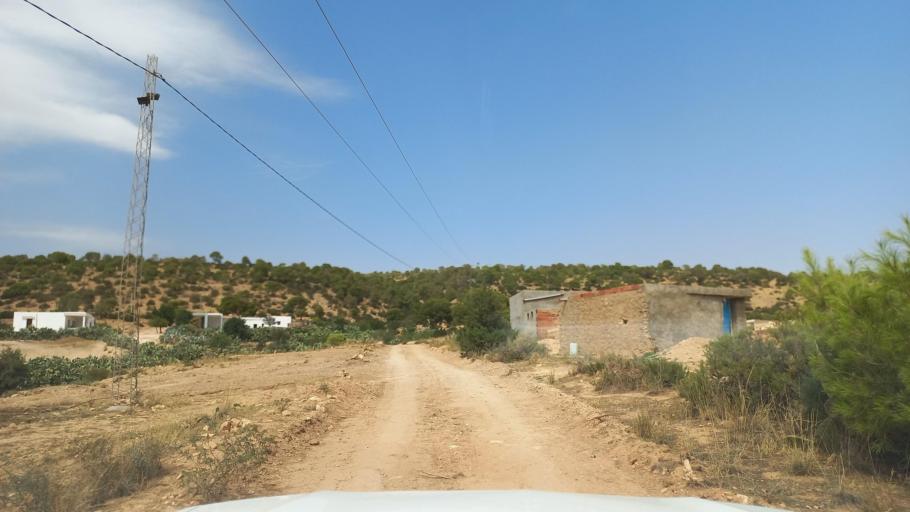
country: TN
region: Al Qasrayn
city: Kasserine
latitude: 35.3728
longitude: 8.8911
